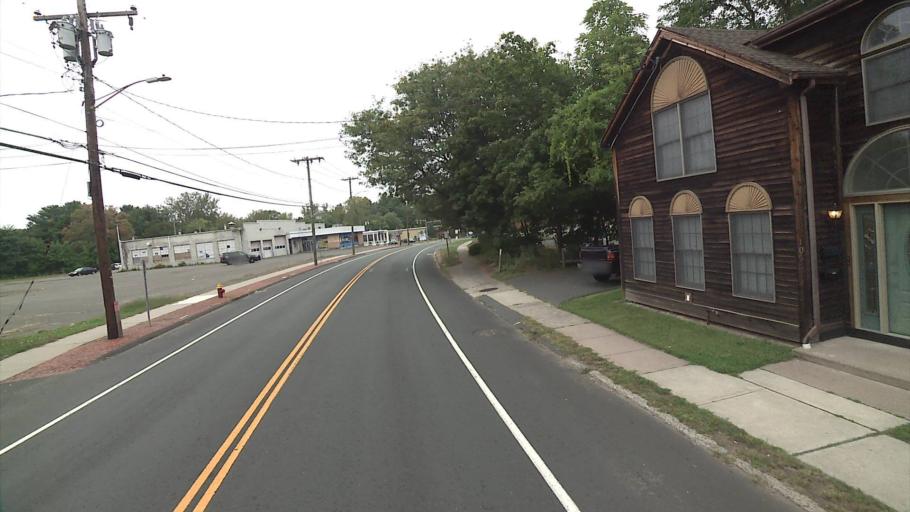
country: US
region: Connecticut
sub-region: Hartford County
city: Windsor
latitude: 41.8552
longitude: -72.6485
